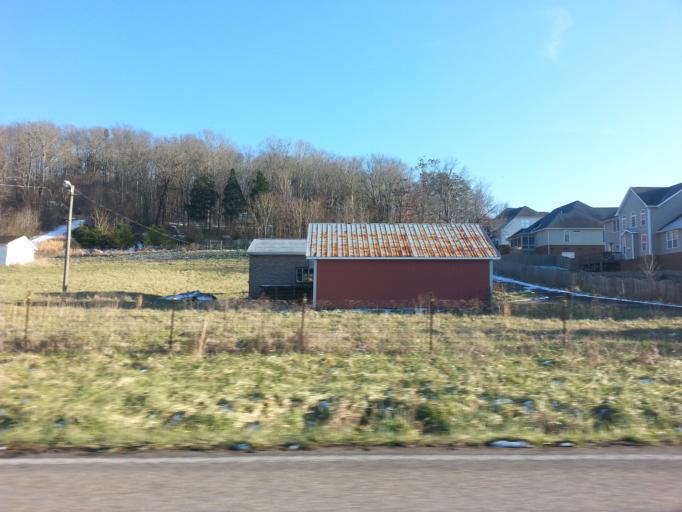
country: US
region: Tennessee
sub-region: Knox County
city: Farragut
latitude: 35.9645
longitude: -84.0878
